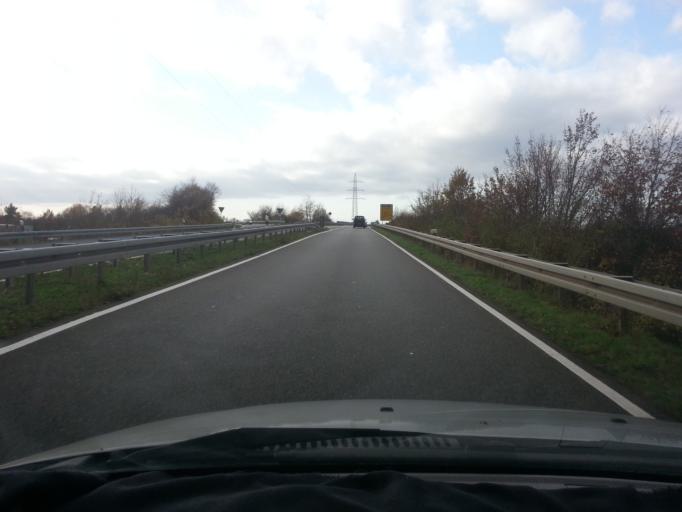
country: DE
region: Baden-Wuerttemberg
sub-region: Karlsruhe Region
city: Leimen
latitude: 49.3682
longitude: 8.6761
